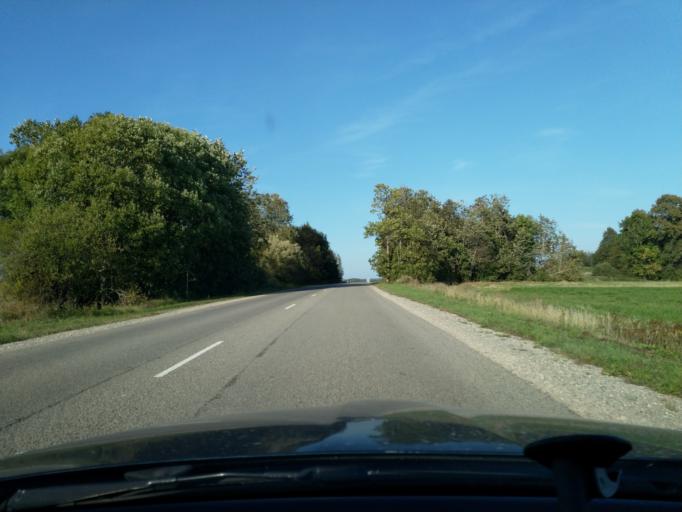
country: LV
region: Aizpute
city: Aizpute
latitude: 56.8305
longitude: 21.7477
